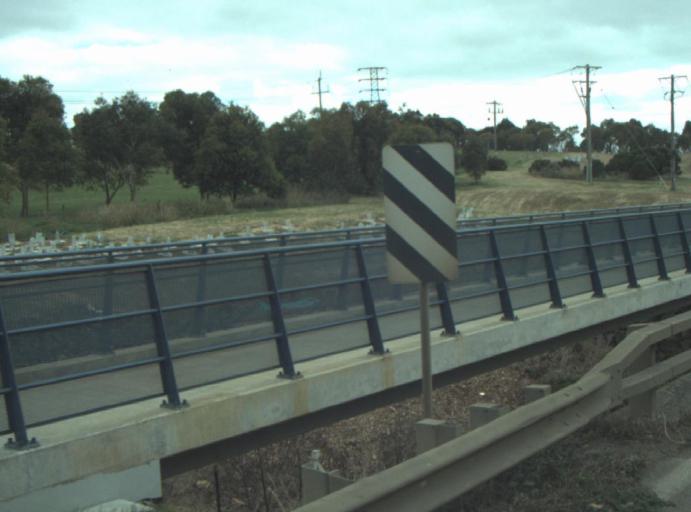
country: AU
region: Victoria
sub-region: Greater Geelong
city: Wandana Heights
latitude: -38.2033
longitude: 144.3027
